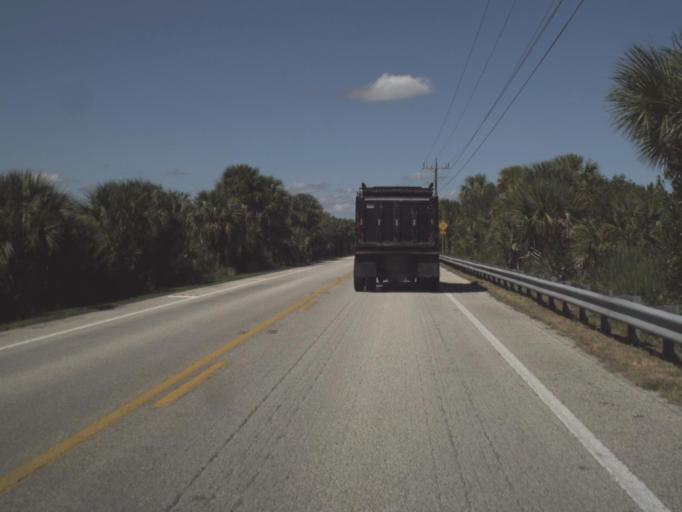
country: US
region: Florida
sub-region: Collier County
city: Marco
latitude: 25.9346
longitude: -81.4509
